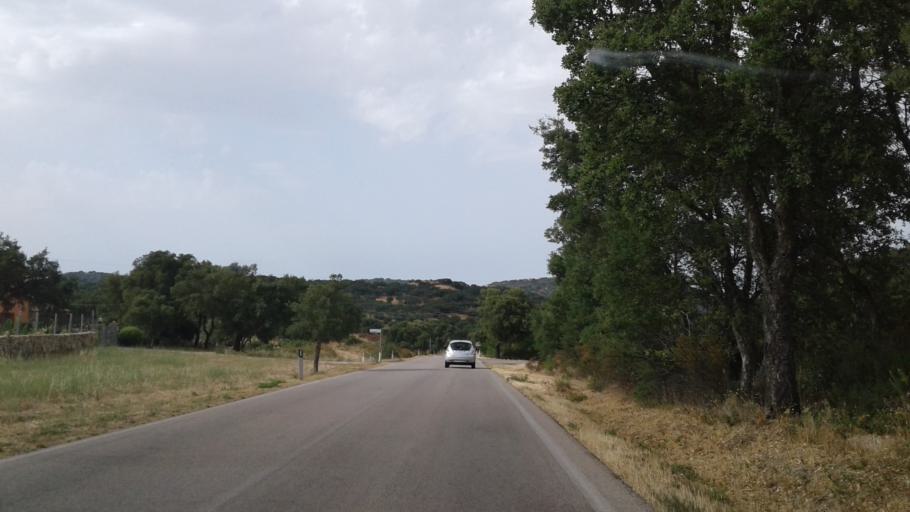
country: IT
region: Sardinia
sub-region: Provincia di Olbia-Tempio
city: Sant'Antonio di Gallura
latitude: 40.9561
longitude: 9.2945
